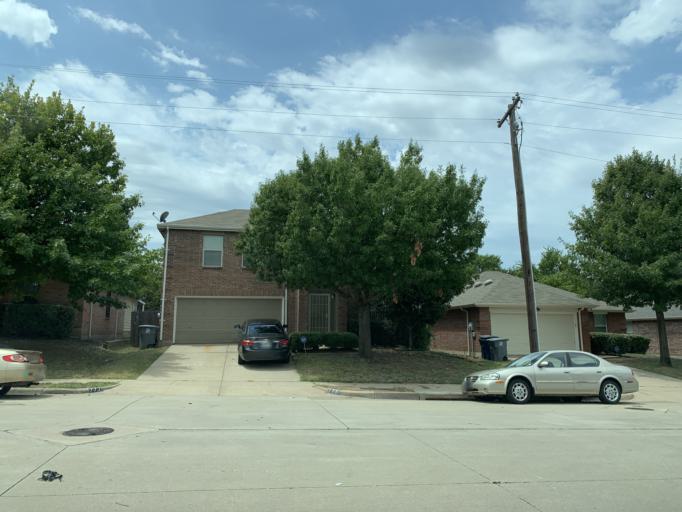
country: US
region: Texas
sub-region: Dallas County
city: DeSoto
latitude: 32.6545
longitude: -96.8138
